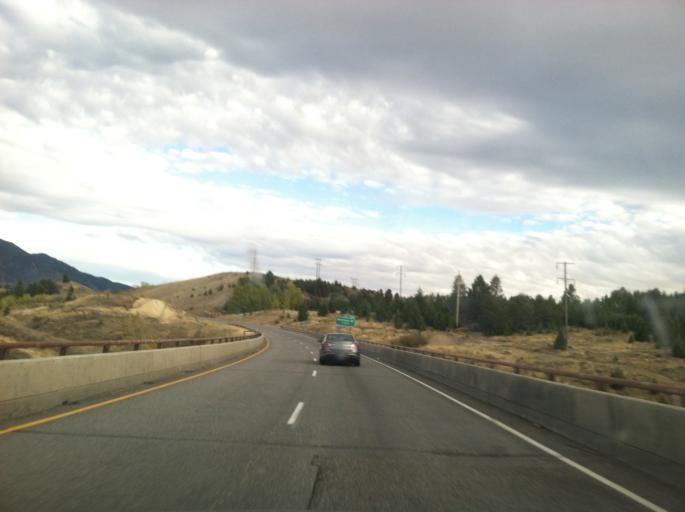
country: US
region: Montana
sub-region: Silver Bow County
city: Butte
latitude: 45.9973
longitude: -112.5669
